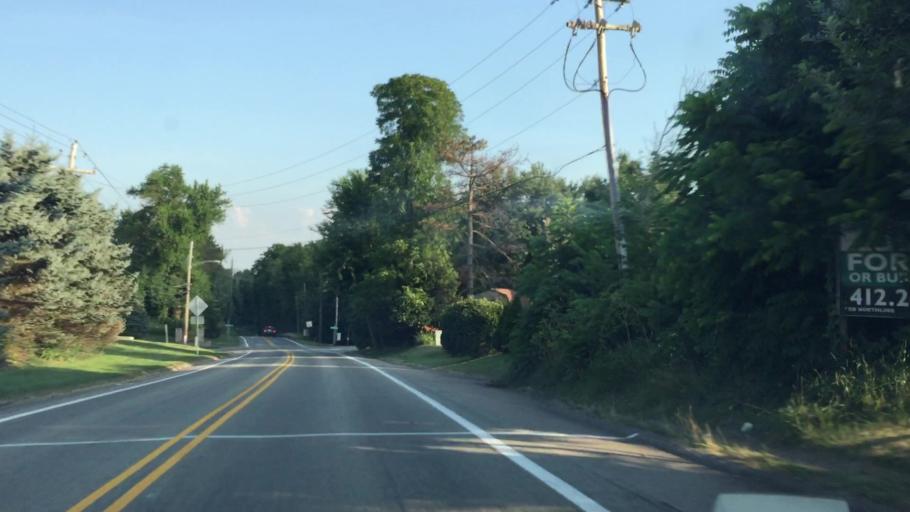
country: US
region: Pennsylvania
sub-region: Allegheny County
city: Bridgeville
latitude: 40.3279
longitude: -80.1250
